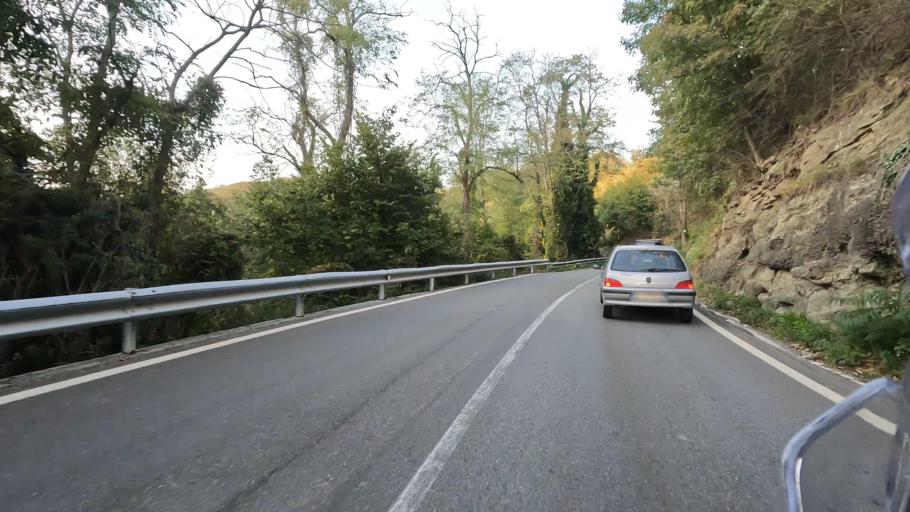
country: IT
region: Liguria
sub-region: Provincia di Savona
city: Osteria dei Cacciatori-Stella
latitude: 44.4220
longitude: 8.4752
